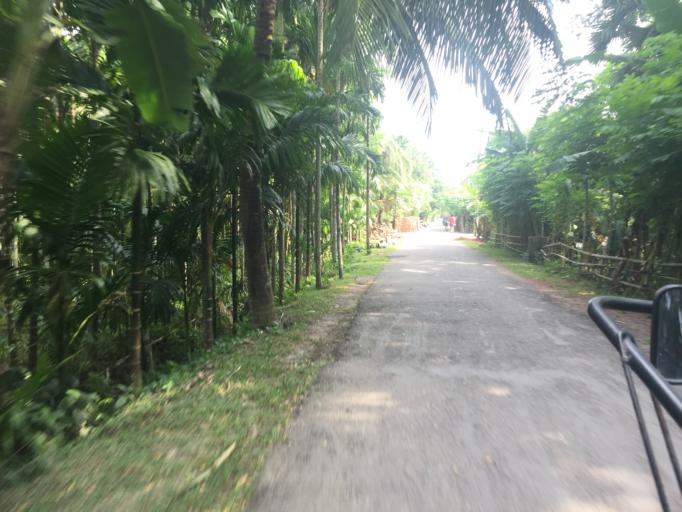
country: BD
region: Barisal
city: Mathba
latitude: 22.2418
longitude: 89.9144
